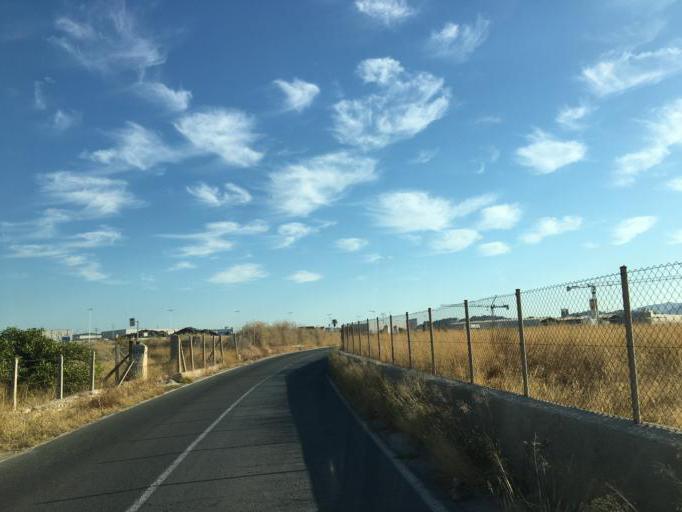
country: ES
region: Murcia
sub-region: Murcia
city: Murcia
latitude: 38.0344
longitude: -1.1196
